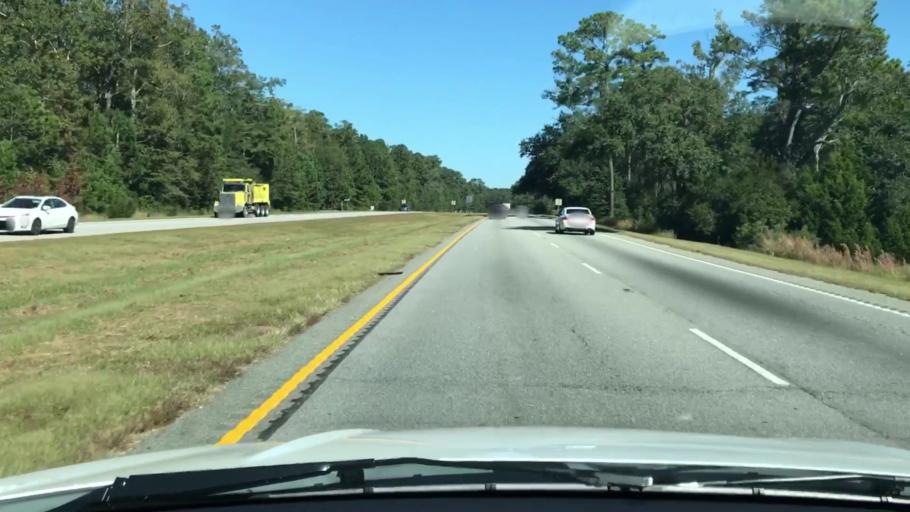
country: US
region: South Carolina
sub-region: Beaufort County
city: Laurel Bay
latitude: 32.3685
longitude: -80.8575
